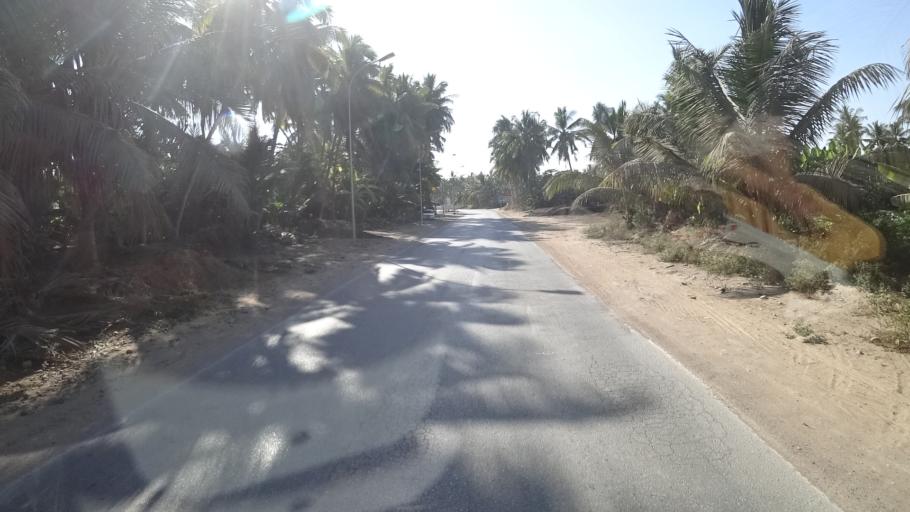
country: OM
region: Zufar
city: Salalah
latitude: 17.0118
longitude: 54.1123
